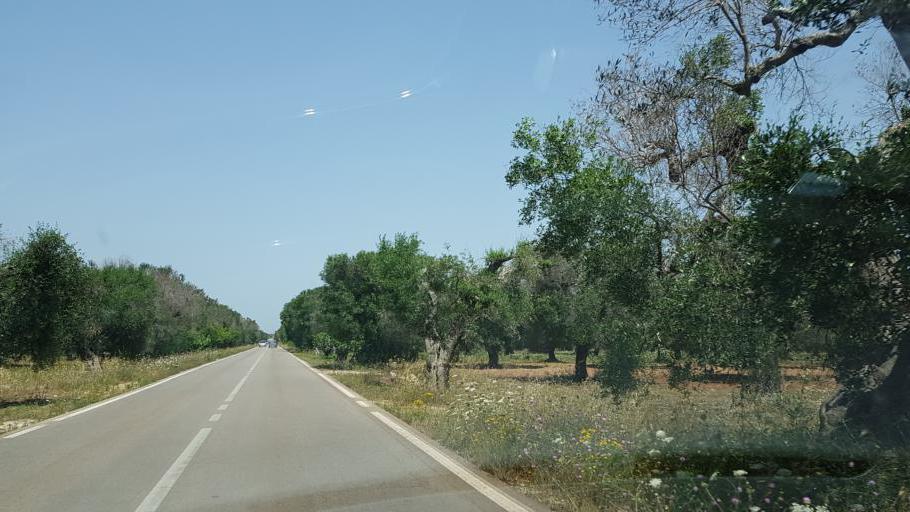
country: IT
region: Apulia
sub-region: Provincia di Lecce
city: Veglie
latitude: 40.3159
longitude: 17.9221
